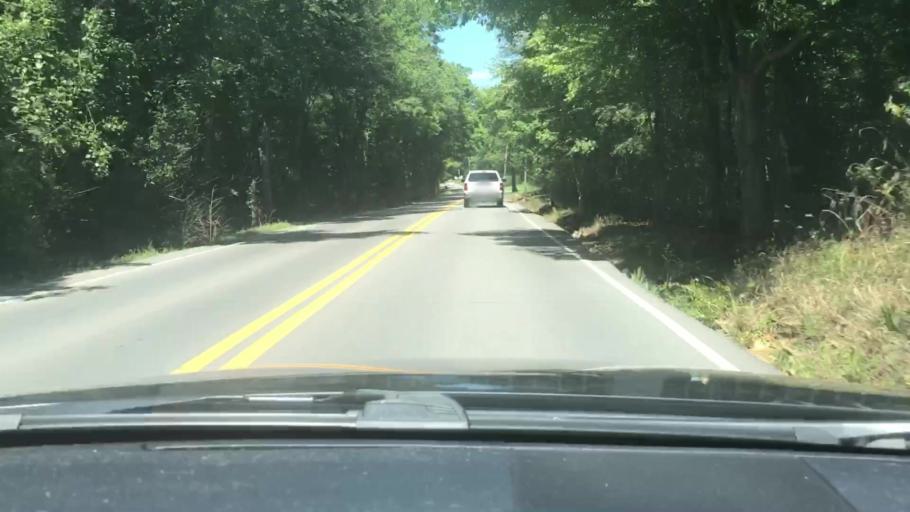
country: US
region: Tennessee
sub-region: Sumner County
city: Gallatin
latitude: 36.4464
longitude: -86.5324
